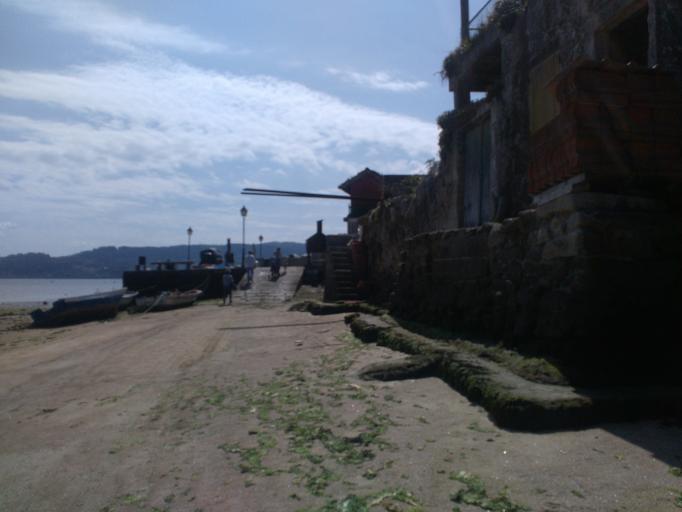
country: ES
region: Galicia
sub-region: Provincia de Pontevedra
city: Combarro
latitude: 42.4328
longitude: -8.7047
